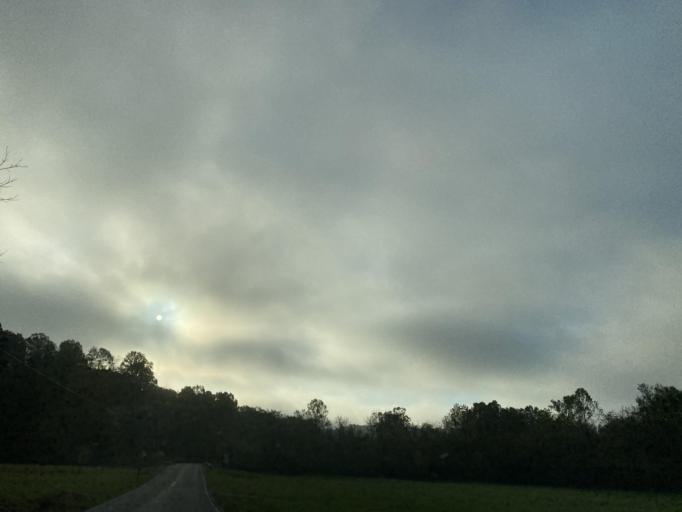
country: US
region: Kentucky
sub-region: Pendleton County
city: Falmouth
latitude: 38.7252
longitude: -84.3026
